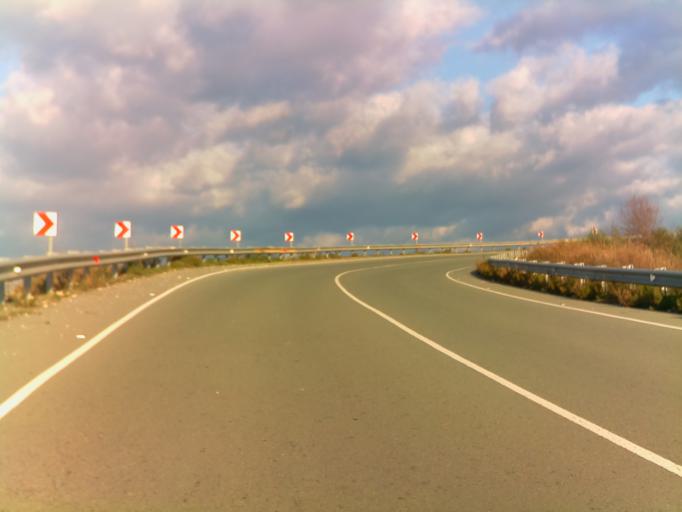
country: CY
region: Pafos
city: Pegeia
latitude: 34.8920
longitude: 32.3536
